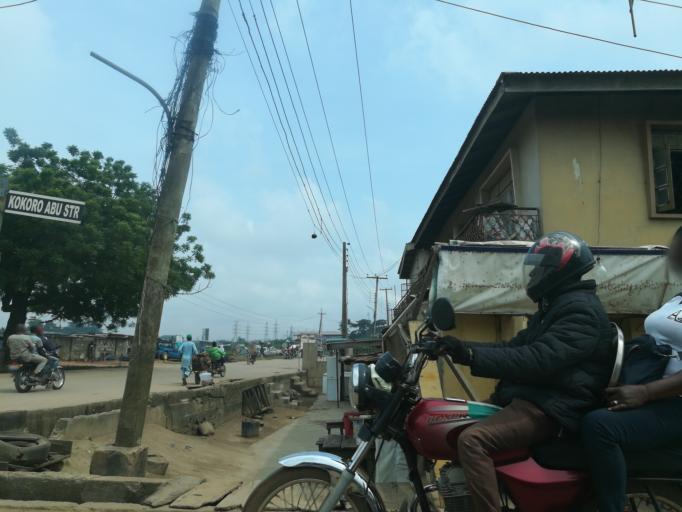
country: NG
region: Lagos
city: Ikorodu
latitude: 6.6198
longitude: 3.5074
